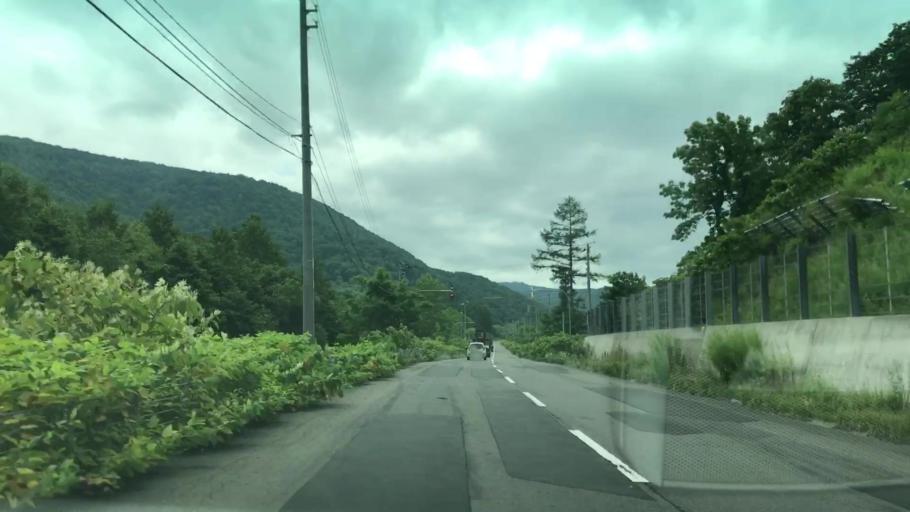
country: JP
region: Hokkaido
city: Yoichi
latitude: 43.0352
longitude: 140.8636
